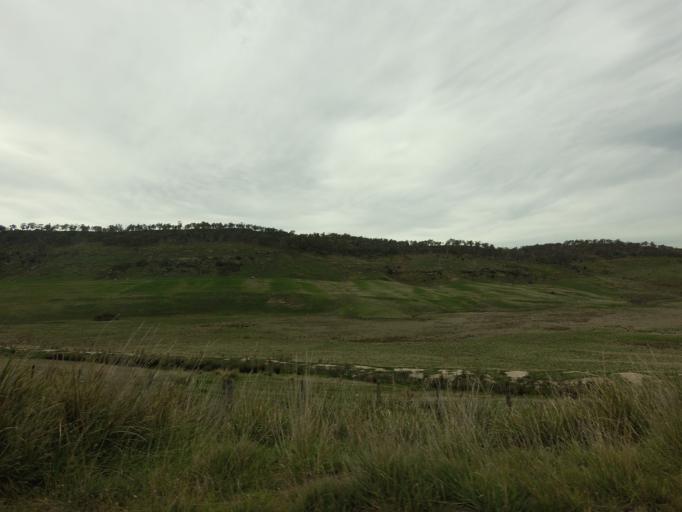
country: AU
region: Tasmania
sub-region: Derwent Valley
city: New Norfolk
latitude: -42.3988
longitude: 146.9189
